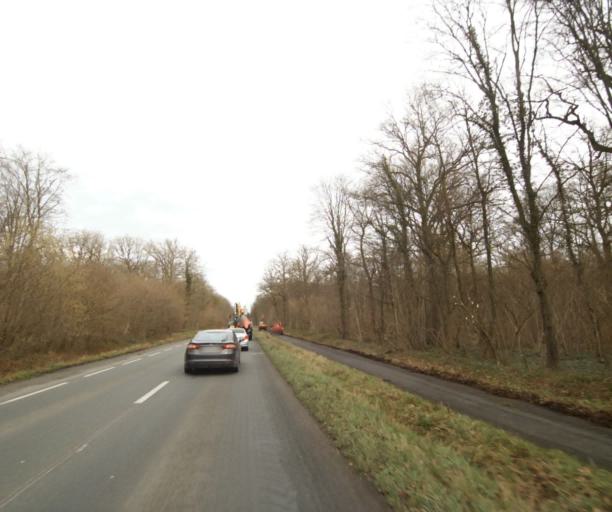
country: BE
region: Wallonia
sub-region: Province du Hainaut
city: Peruwelz
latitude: 50.4874
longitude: 3.6035
